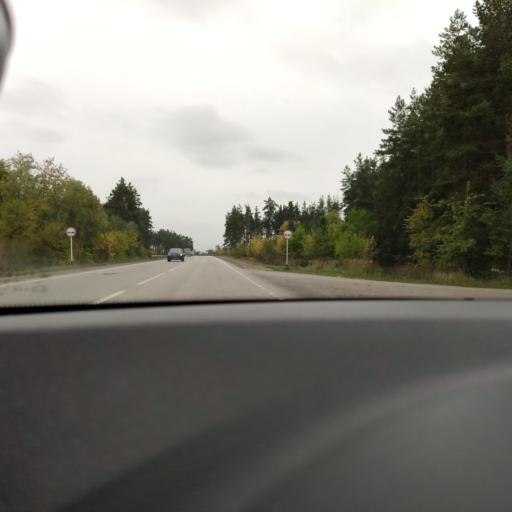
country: RU
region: Samara
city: Mirnyy
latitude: 53.5440
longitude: 50.2964
